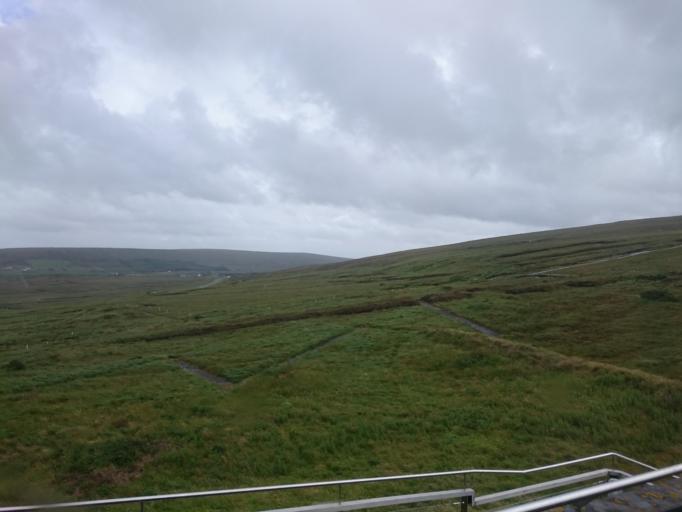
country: IE
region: Connaught
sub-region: Maigh Eo
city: Crossmolina
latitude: 54.3071
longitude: -9.4576
